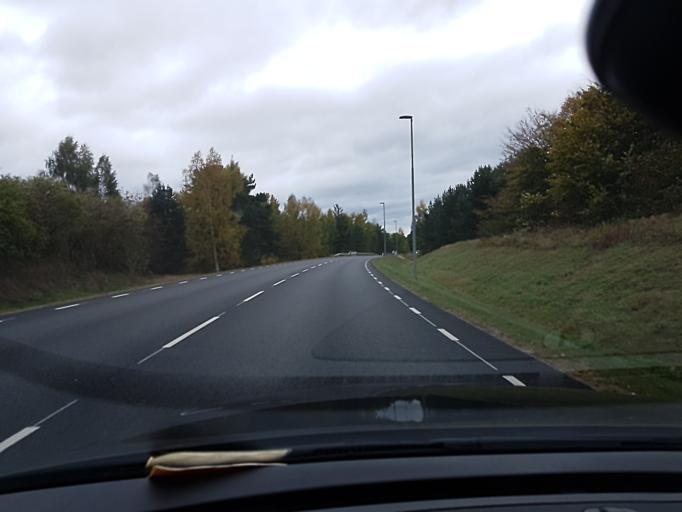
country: SE
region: Kronoberg
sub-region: Vaxjo Kommun
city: Vaexjoe
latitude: 56.9111
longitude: 14.7997
